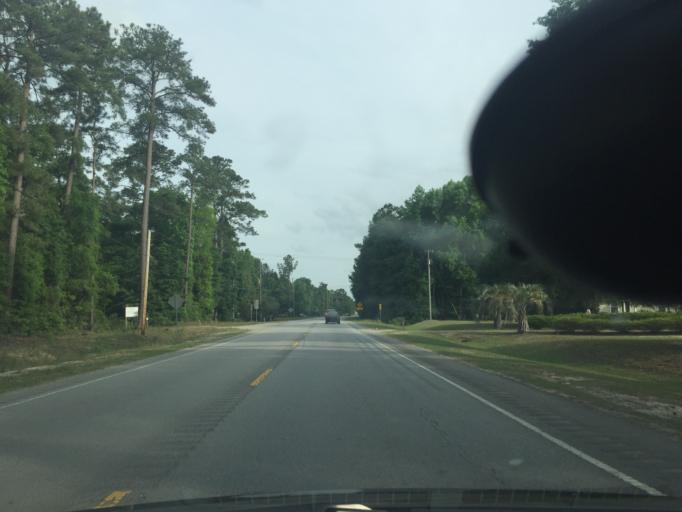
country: US
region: Georgia
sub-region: Bryan County
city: Richmond Hill
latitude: 32.0353
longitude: -81.3257
